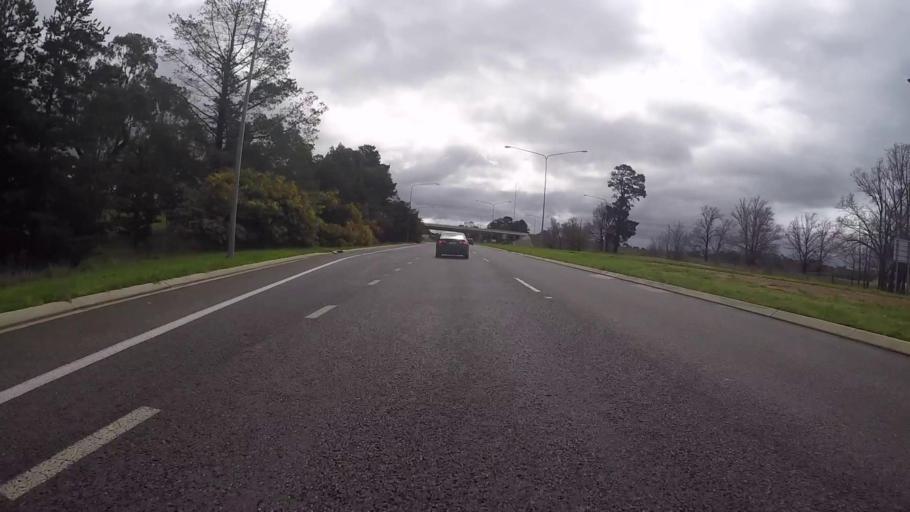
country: AU
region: Australian Capital Territory
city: Kaleen
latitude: -35.2278
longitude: 149.1232
